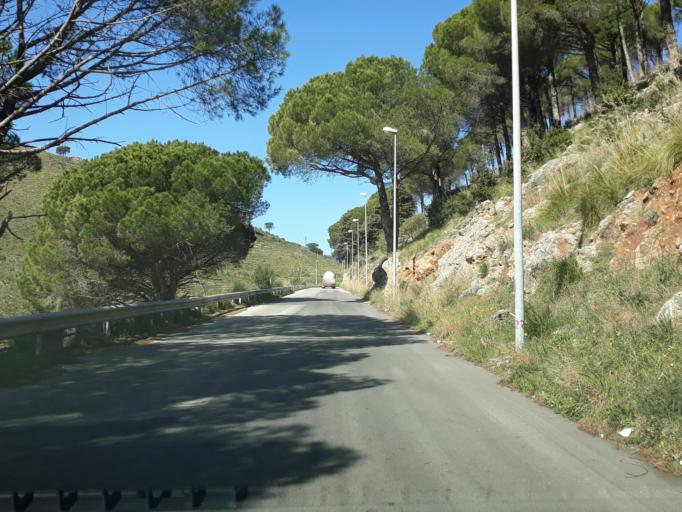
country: IT
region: Sicily
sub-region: Palermo
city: Monreale
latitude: 38.0797
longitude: 13.2751
